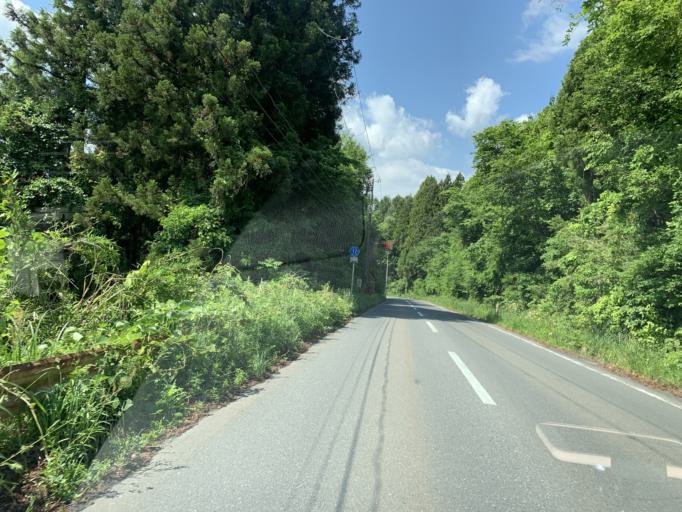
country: JP
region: Miyagi
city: Furukawa
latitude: 38.7135
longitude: 140.9431
